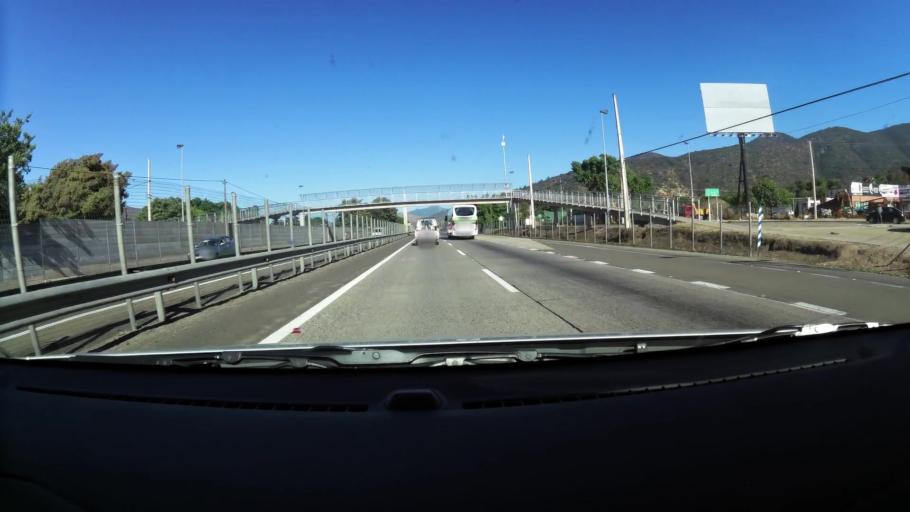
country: CL
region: Santiago Metropolitan
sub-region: Provincia de Chacabuco
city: Lampa
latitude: -33.4099
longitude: -71.0630
